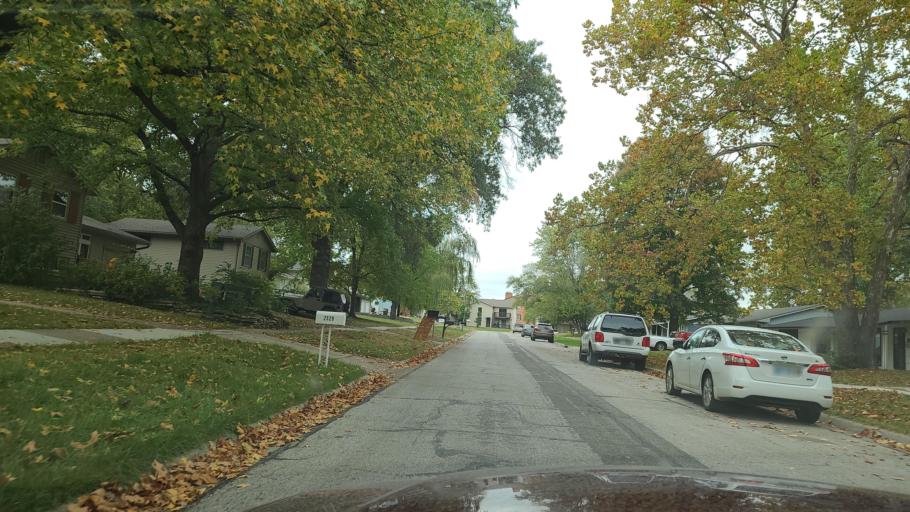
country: US
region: Kansas
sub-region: Douglas County
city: Lawrence
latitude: 38.9373
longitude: -95.2439
